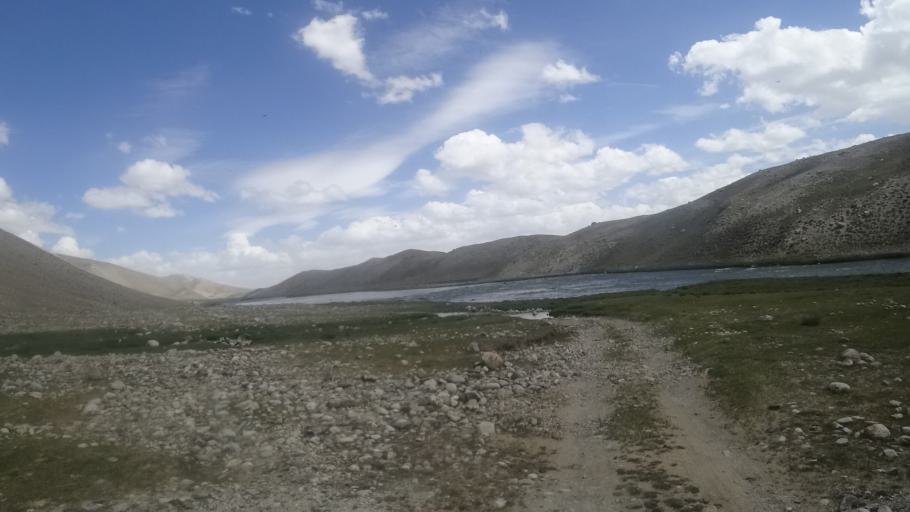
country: TJ
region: Gorno-Badakhshan
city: Murghob
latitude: 37.4747
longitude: 73.4554
